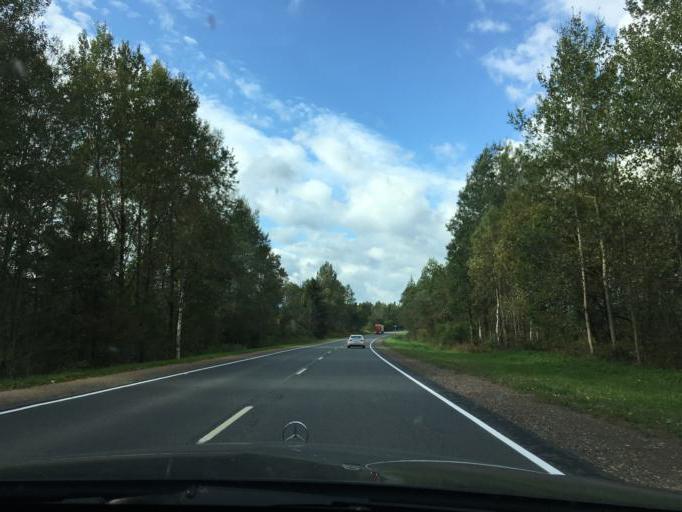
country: RU
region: Tverskaya
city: Toropets
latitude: 56.3324
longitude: 31.2918
